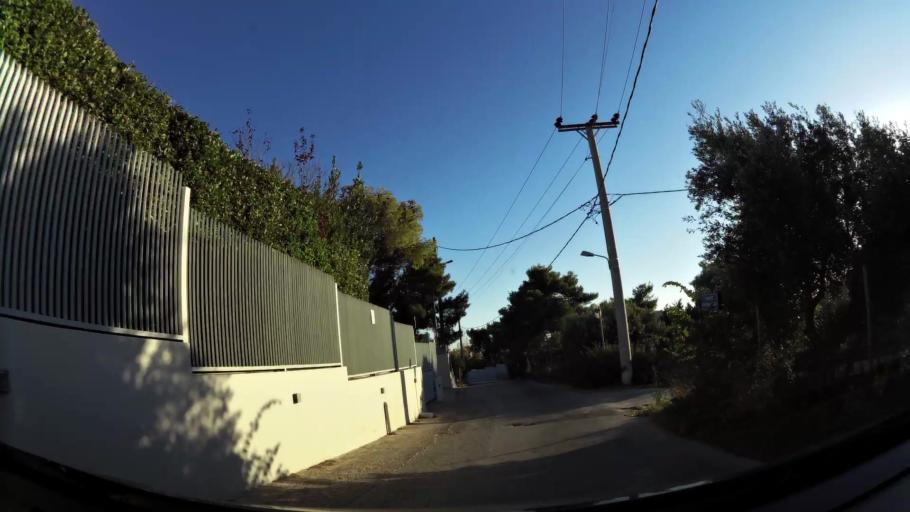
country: GR
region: Attica
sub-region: Nomarchia Athinas
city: Penteli
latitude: 38.0422
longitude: 23.8575
